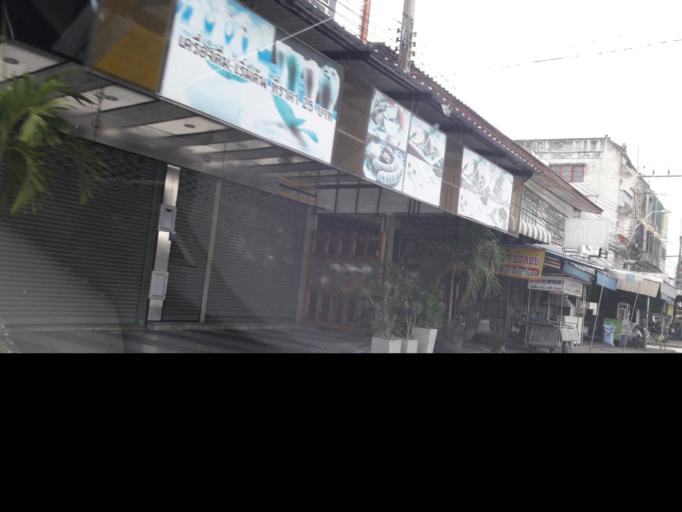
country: TH
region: Ratchaburi
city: Ratchaburi
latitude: 13.5278
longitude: 99.8182
